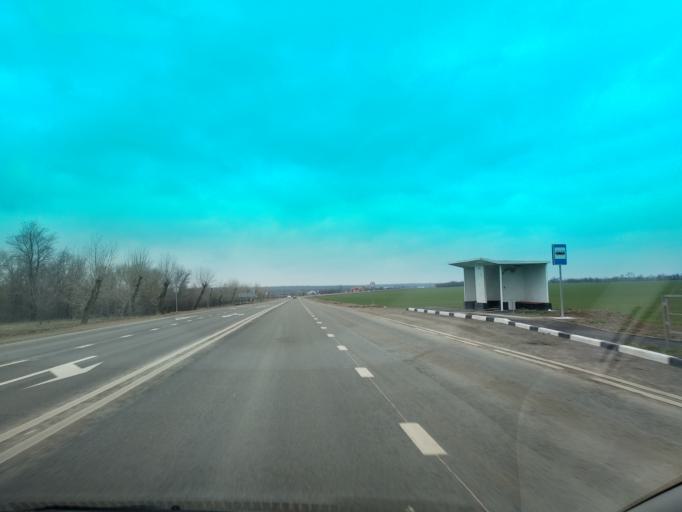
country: RU
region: Krasnodarskiy
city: Novomalorossiyskaya
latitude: 45.7068
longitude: 39.8458
